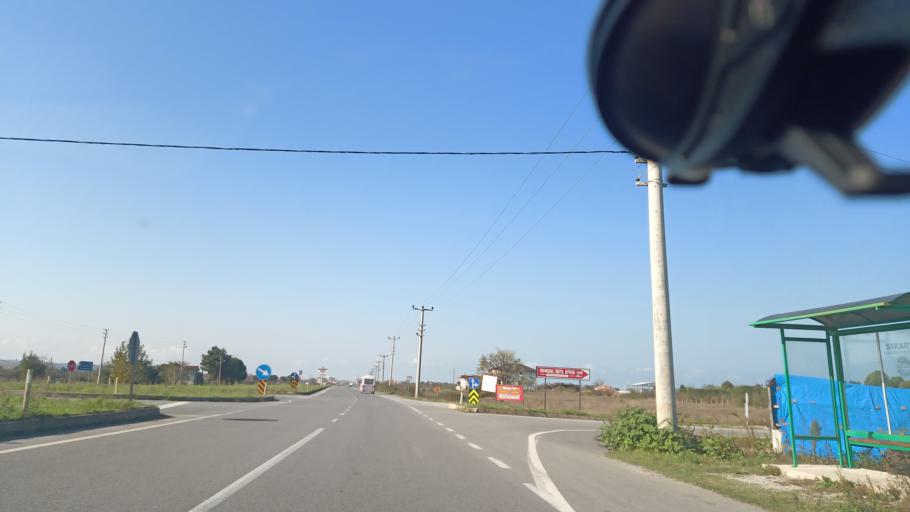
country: TR
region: Sakarya
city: Karasu
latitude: 41.0825
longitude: 30.7637
